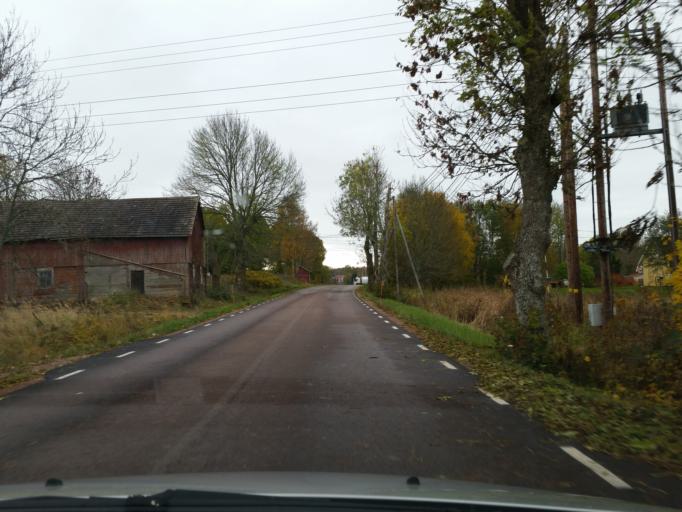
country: AX
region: Alands landsbygd
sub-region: Lemland
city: Lemland
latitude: 60.0732
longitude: 20.0843
